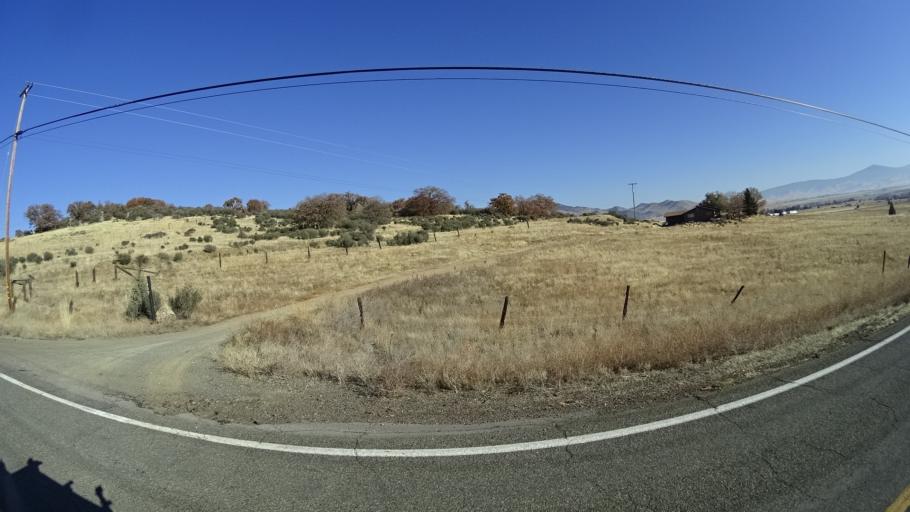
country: US
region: California
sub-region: Siskiyou County
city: Yreka
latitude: 41.7376
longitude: -122.6030
